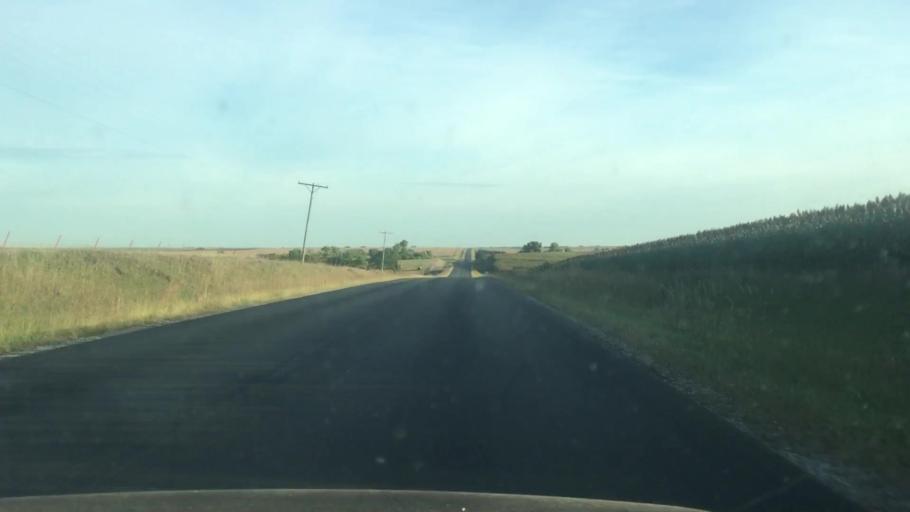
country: US
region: Kansas
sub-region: Marshall County
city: Marysville
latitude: 39.8928
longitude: -96.6010
